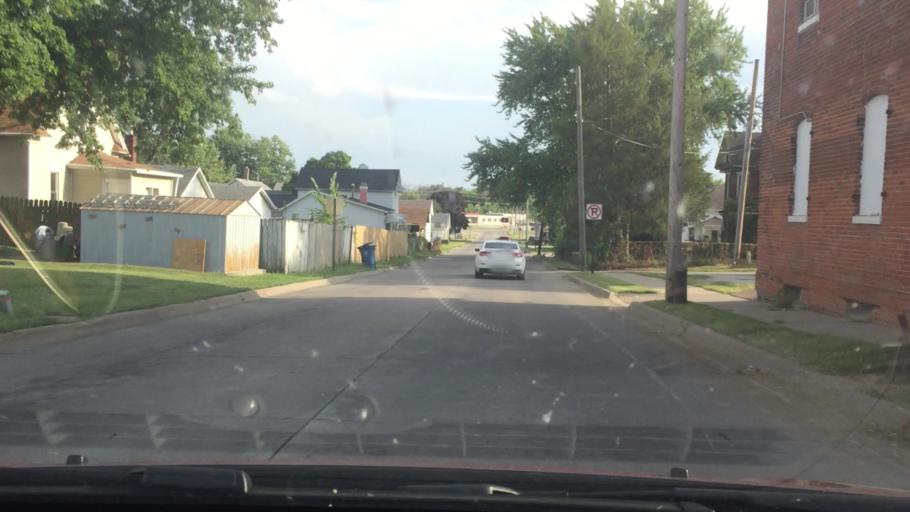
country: US
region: Iowa
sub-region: Muscatine County
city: Muscatine
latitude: 41.4153
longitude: -91.0590
